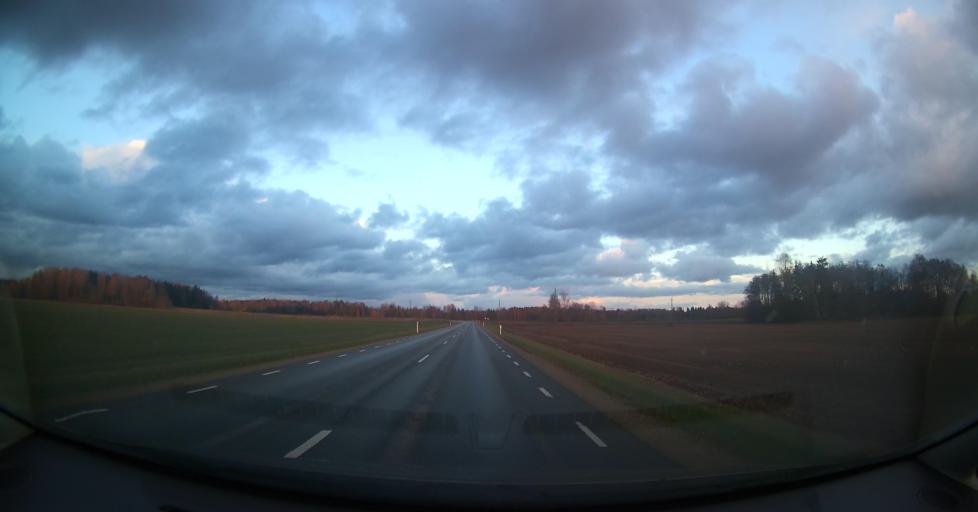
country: EE
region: Harju
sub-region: Anija vald
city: Kehra
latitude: 59.2563
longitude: 25.3369
